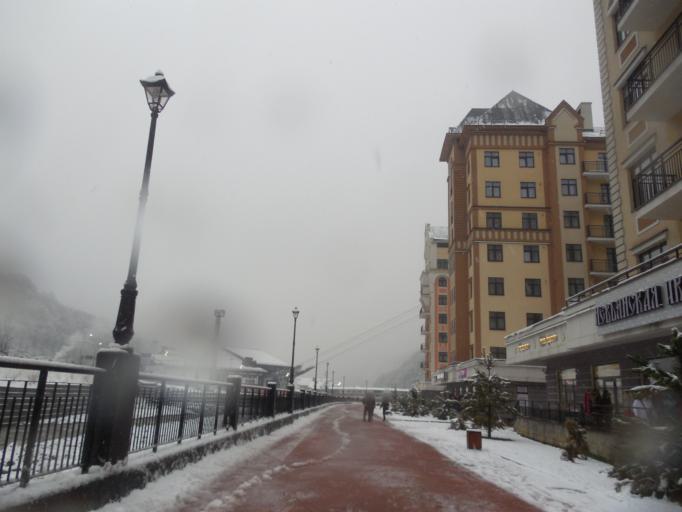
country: RU
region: Krasnodarskiy
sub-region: Sochi City
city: Krasnaya Polyana
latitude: 43.6753
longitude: 40.2874
